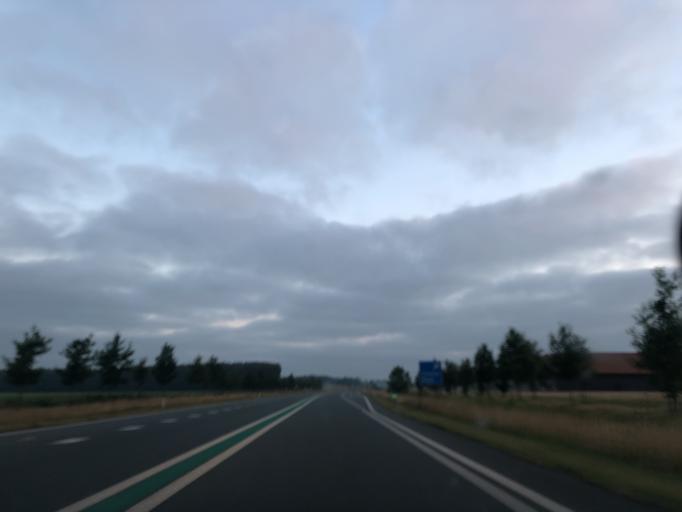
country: NL
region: Drenthe
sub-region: Gemeente Aa en Hunze
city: Anloo
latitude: 52.9938
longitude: 6.7585
